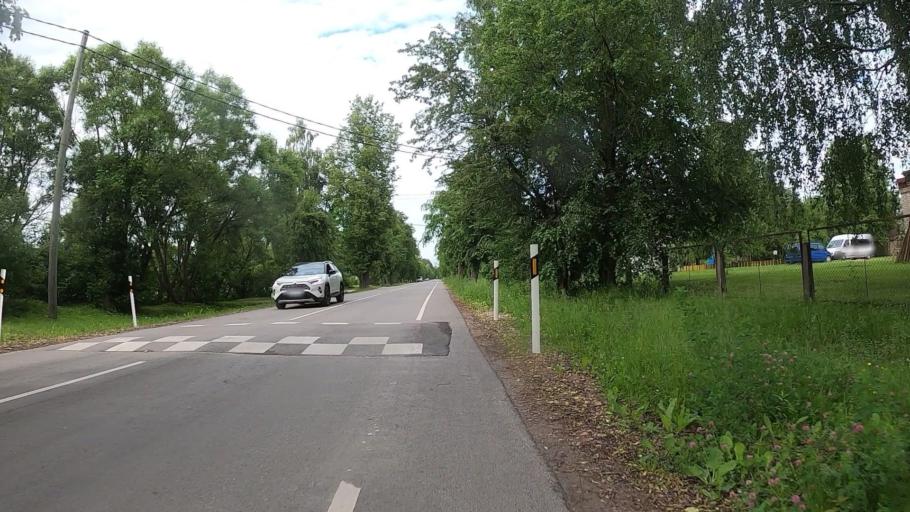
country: LV
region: Jelgava
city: Jelgava
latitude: 56.6644
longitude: 23.7460
